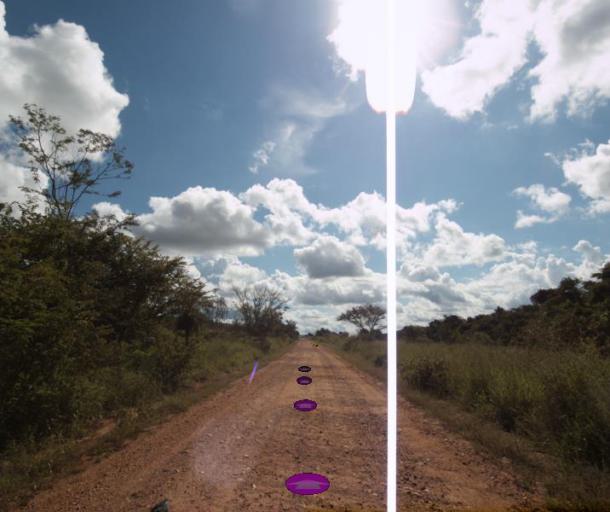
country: BR
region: Goias
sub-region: Jaragua
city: Jaragua
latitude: -15.8212
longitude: -49.2073
